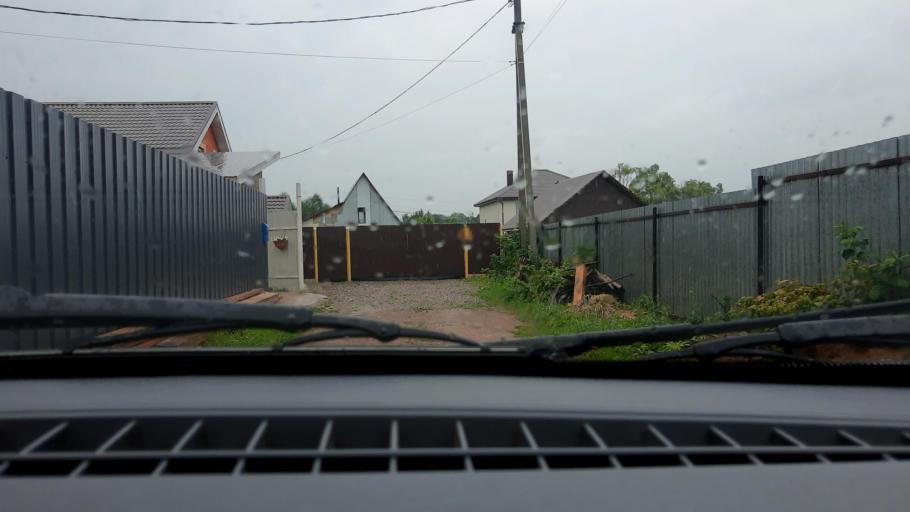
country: RU
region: Bashkortostan
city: Mikhaylovka
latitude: 54.8172
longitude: 55.8492
